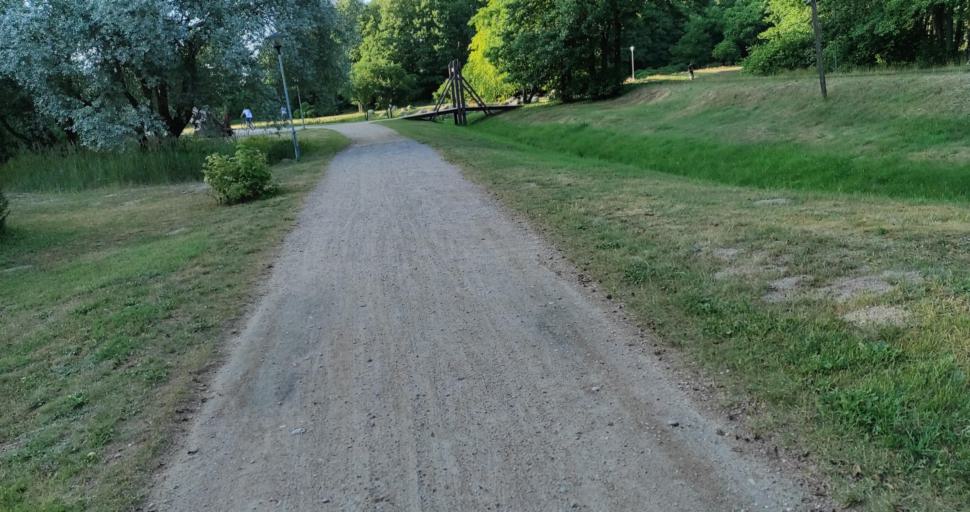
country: LV
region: Ventspils
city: Ventspils
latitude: 57.3859
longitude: 21.5299
